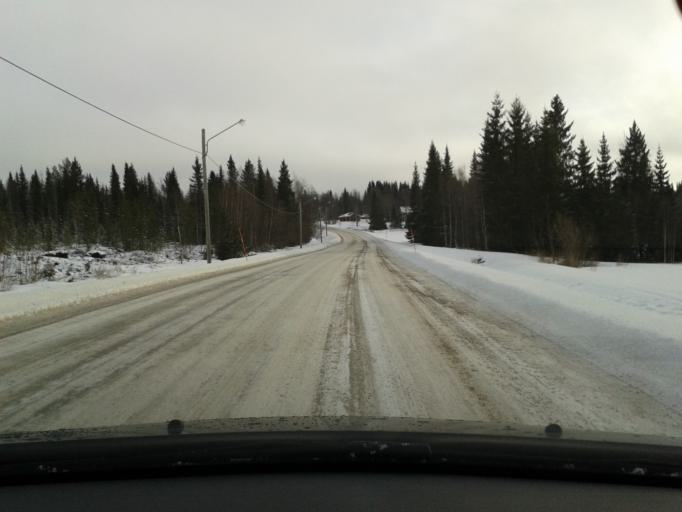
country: SE
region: Vaesterbotten
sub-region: Vilhelmina Kommun
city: Sjoberg
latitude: 64.7942
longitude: 16.0744
